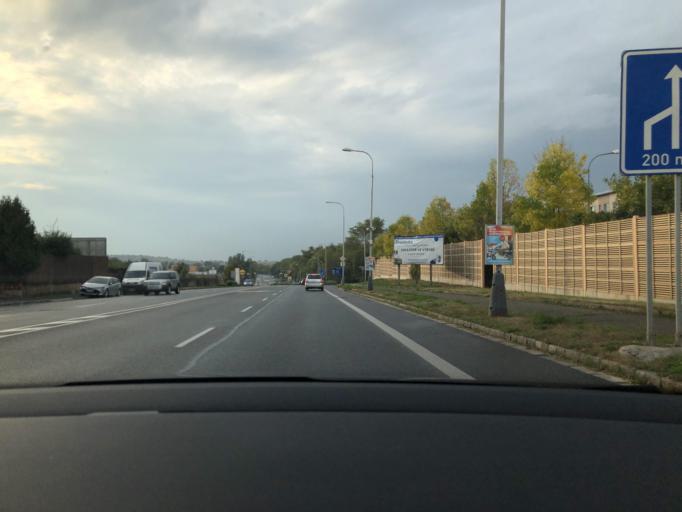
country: CZ
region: Central Bohemia
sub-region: Okres Kolin
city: Kolin
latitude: 50.0310
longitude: 15.1873
